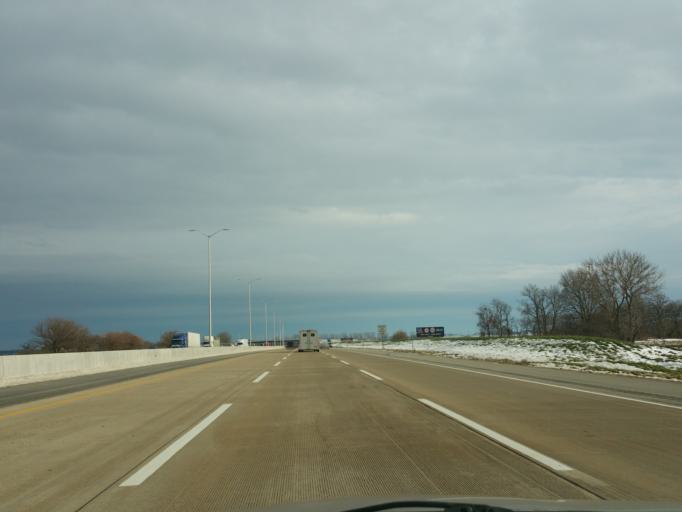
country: US
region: Illinois
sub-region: Boone County
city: Belvidere
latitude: 42.2228
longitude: -88.7581
